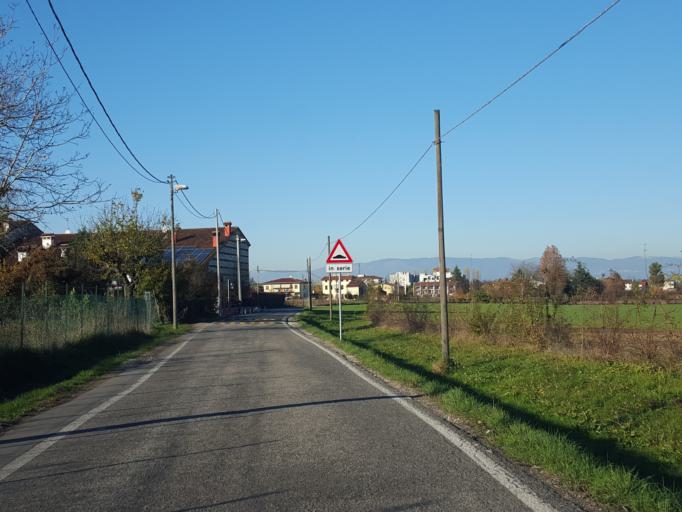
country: IT
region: Veneto
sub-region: Provincia di Vicenza
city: Villaggio Montegrappa
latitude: 45.5363
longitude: 11.6050
